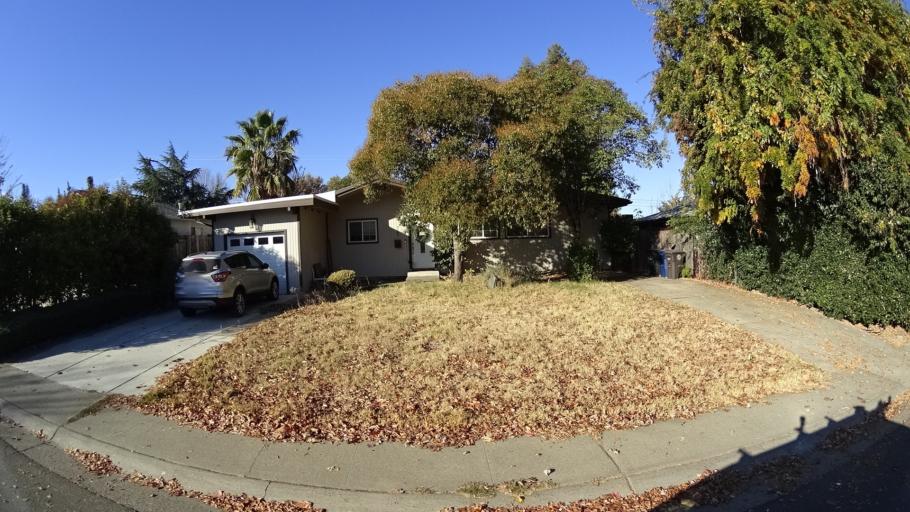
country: US
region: California
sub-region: Sacramento County
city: Fair Oaks
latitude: 38.6693
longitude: -121.2951
